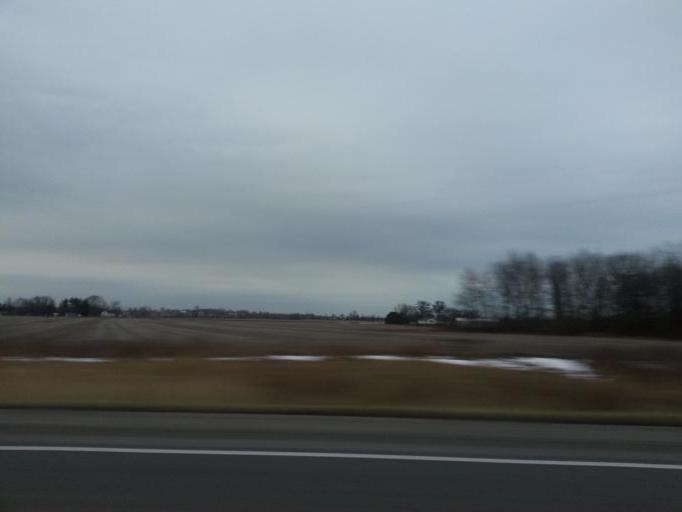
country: US
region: Iowa
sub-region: Linn County
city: Center Point
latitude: 42.1929
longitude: -91.8147
